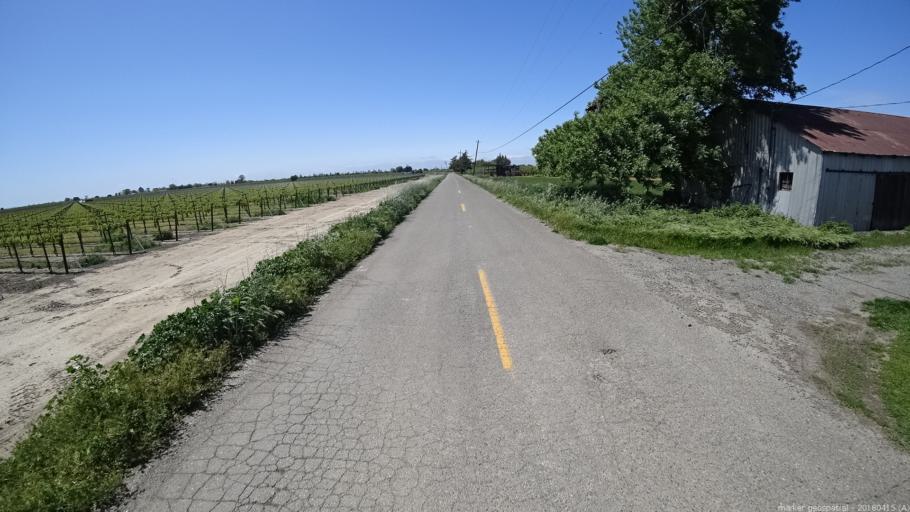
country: US
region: California
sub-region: Sacramento County
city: Walnut Grove
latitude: 38.2953
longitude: -121.5893
